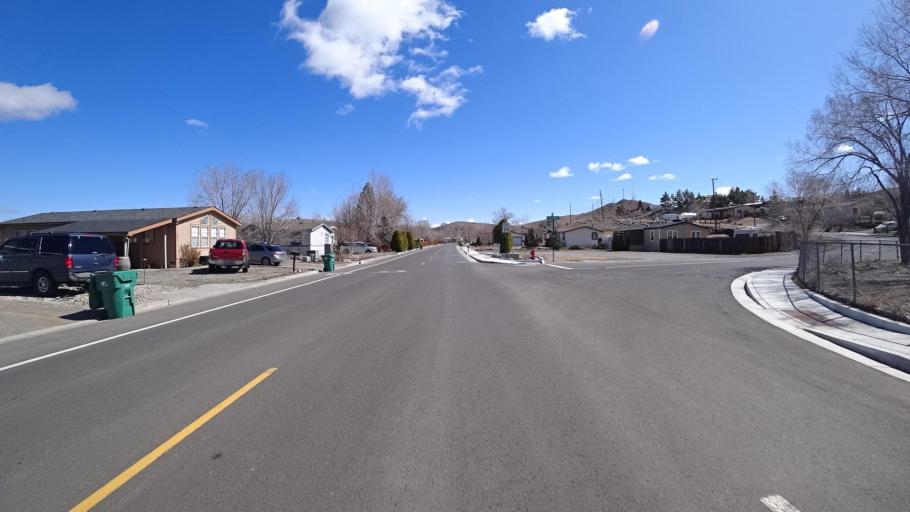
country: US
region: Nevada
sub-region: Washoe County
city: Golden Valley
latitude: 39.5883
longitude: -119.8157
